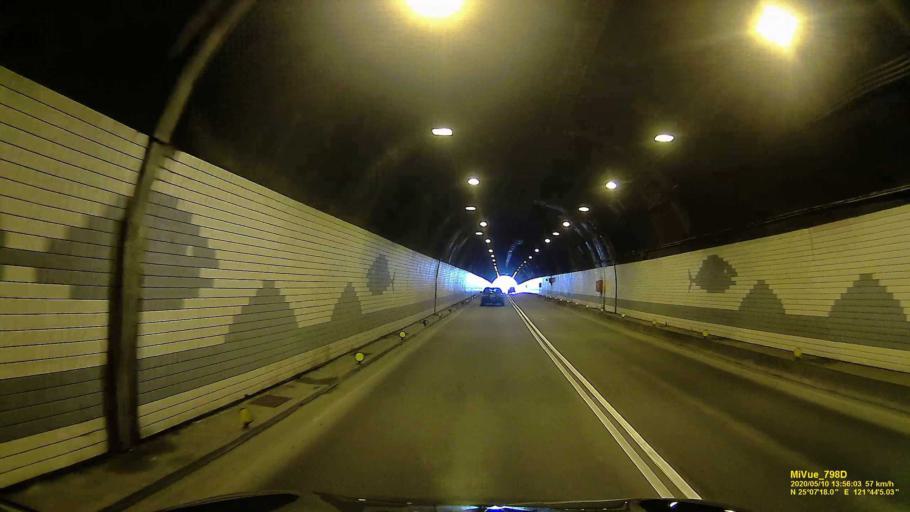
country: TW
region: Taiwan
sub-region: Keelung
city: Keelung
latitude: 25.1208
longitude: 121.7340
